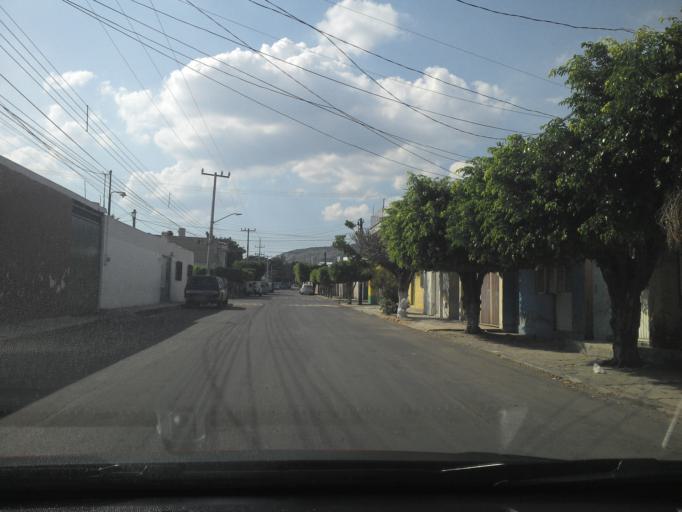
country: MX
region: Jalisco
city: Guadalajara
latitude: 20.6460
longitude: -103.4360
